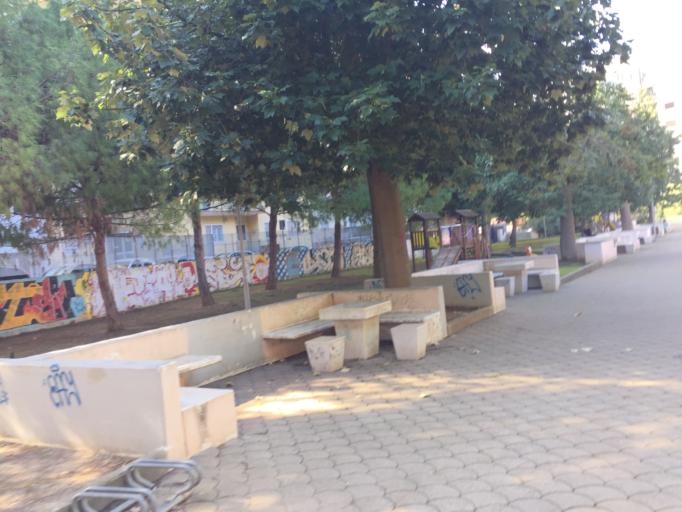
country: IT
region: Apulia
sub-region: Provincia di Bari
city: Bari
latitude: 41.1151
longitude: 16.8661
